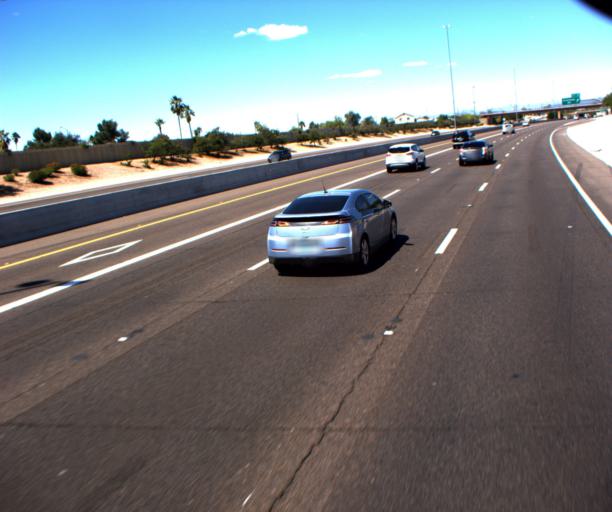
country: US
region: Arizona
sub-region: Maricopa County
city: Paradise Valley
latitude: 33.6196
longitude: -112.0092
